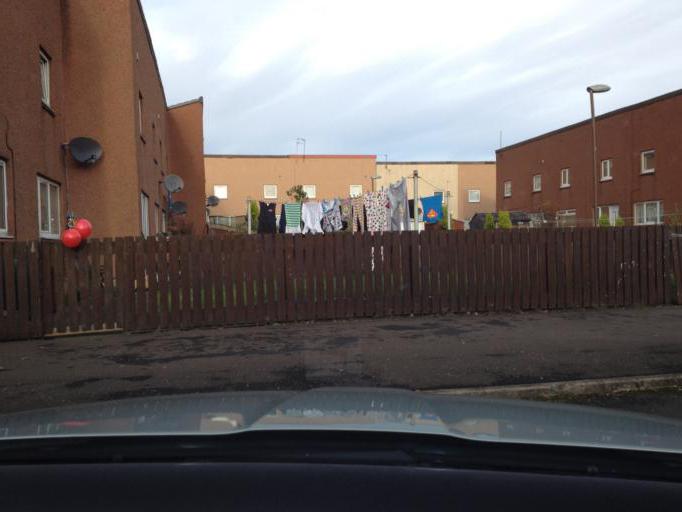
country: GB
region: Scotland
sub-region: West Lothian
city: Livingston
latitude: 55.9086
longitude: -3.5211
